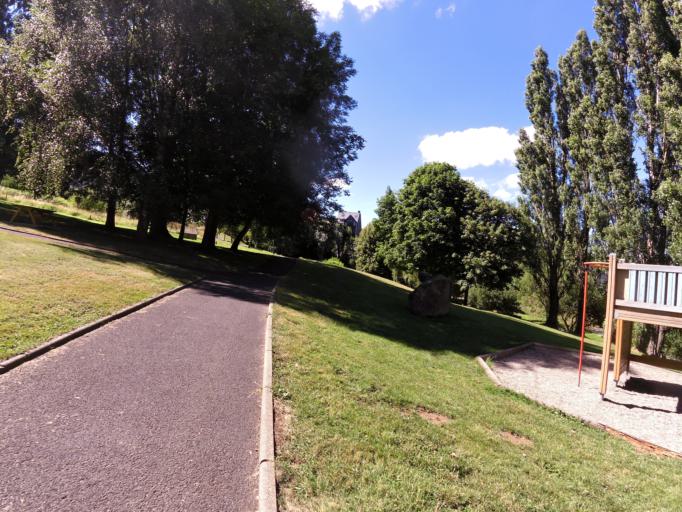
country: FR
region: Auvergne
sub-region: Departement du Puy-de-Dome
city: Mont-Dore
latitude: 45.5107
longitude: 2.9358
